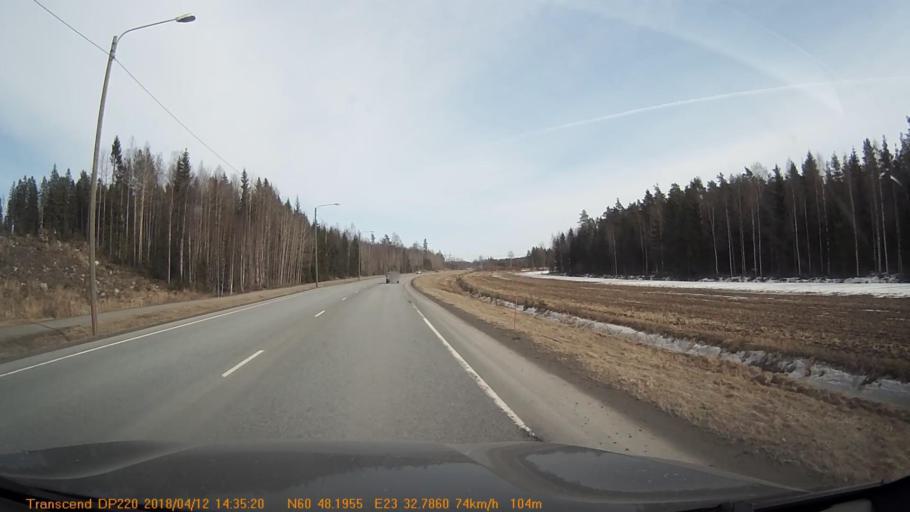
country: FI
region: Haeme
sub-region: Forssa
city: Jokioinen
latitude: 60.8032
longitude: 23.5476
